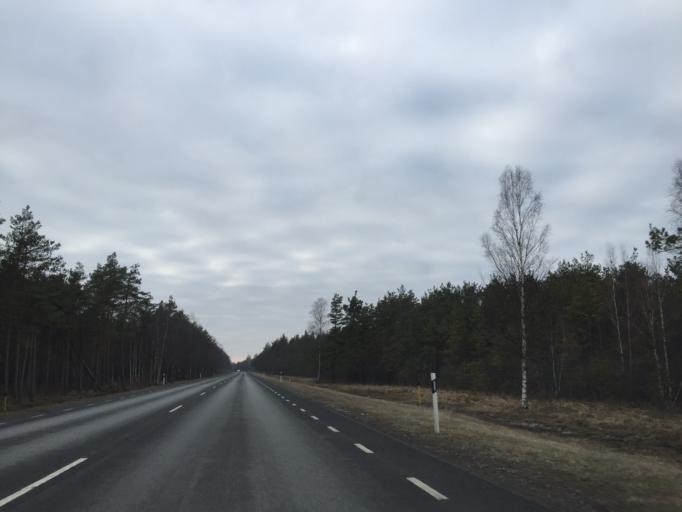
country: EE
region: Saare
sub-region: Orissaare vald
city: Orissaare
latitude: 58.5312
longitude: 22.9838
